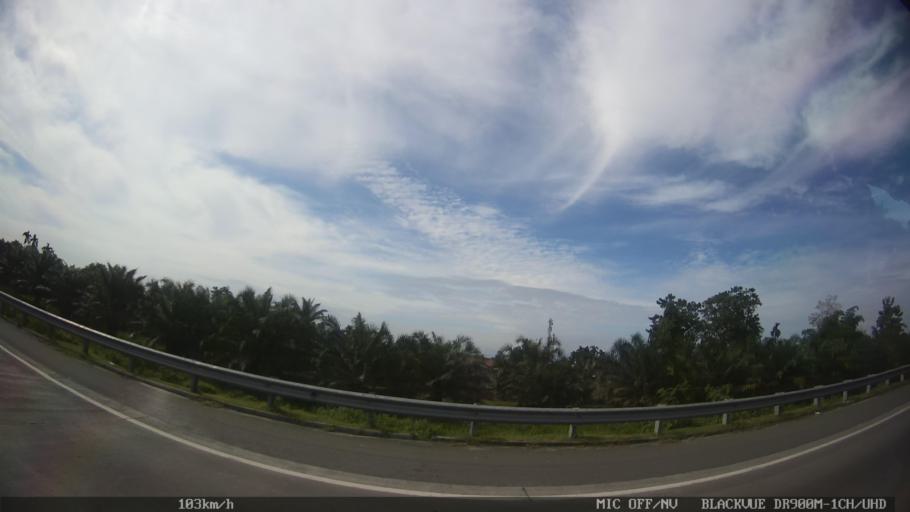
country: ID
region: North Sumatra
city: Sunggal
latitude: 3.6378
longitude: 98.5972
